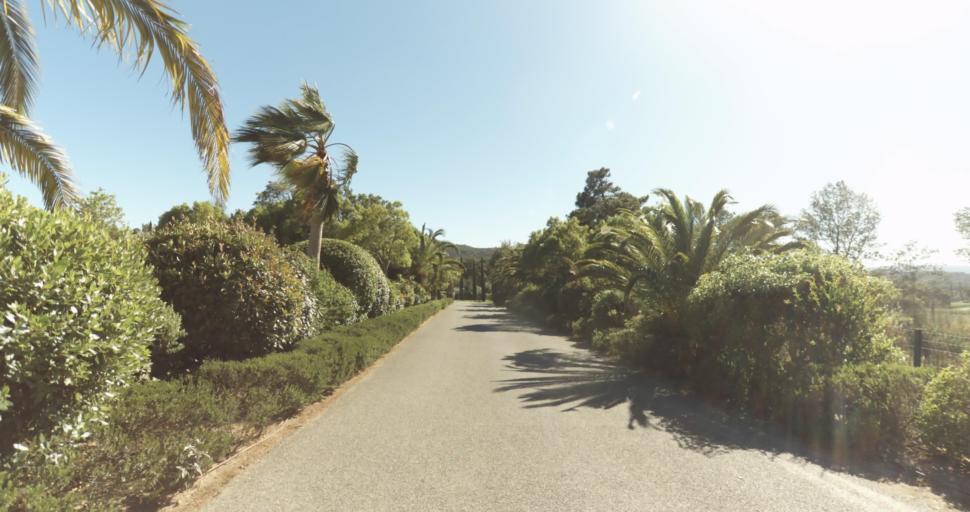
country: FR
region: Provence-Alpes-Cote d'Azur
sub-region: Departement du Var
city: Gassin
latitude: 43.2535
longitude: 6.6003
